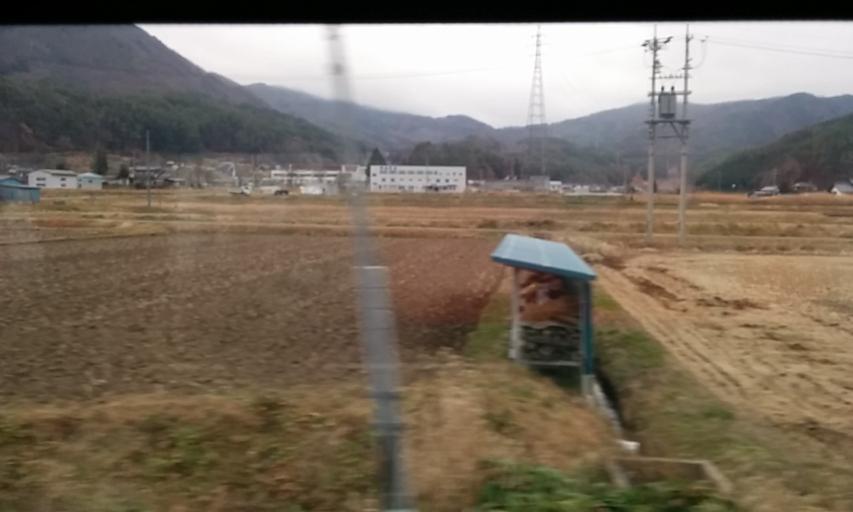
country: JP
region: Nagano
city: Omachi
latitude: 36.4563
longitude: 138.0529
